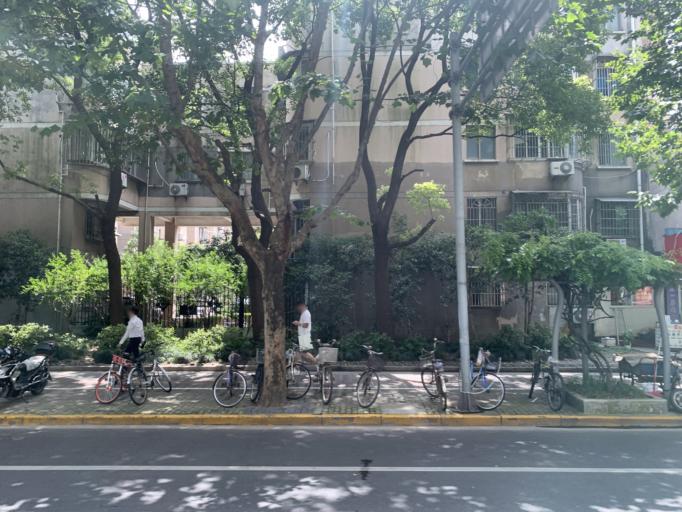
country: CN
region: Shanghai Shi
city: Pudong
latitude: 31.2485
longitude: 121.5603
